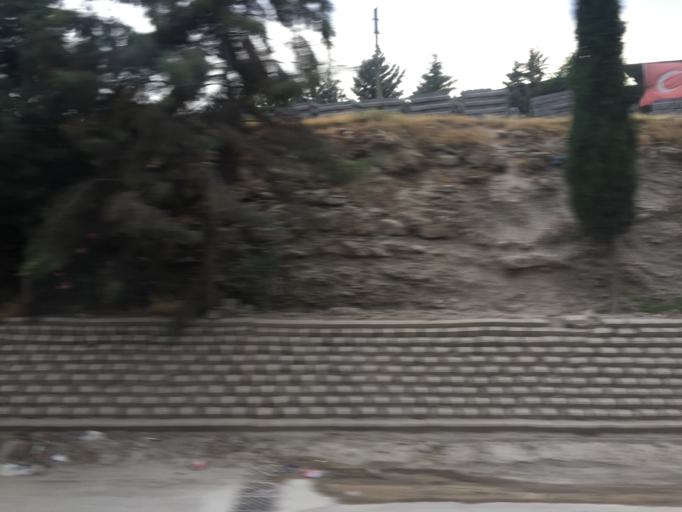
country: TR
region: Gaziantep
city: Gaziantep
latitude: 37.0228
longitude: 37.4282
